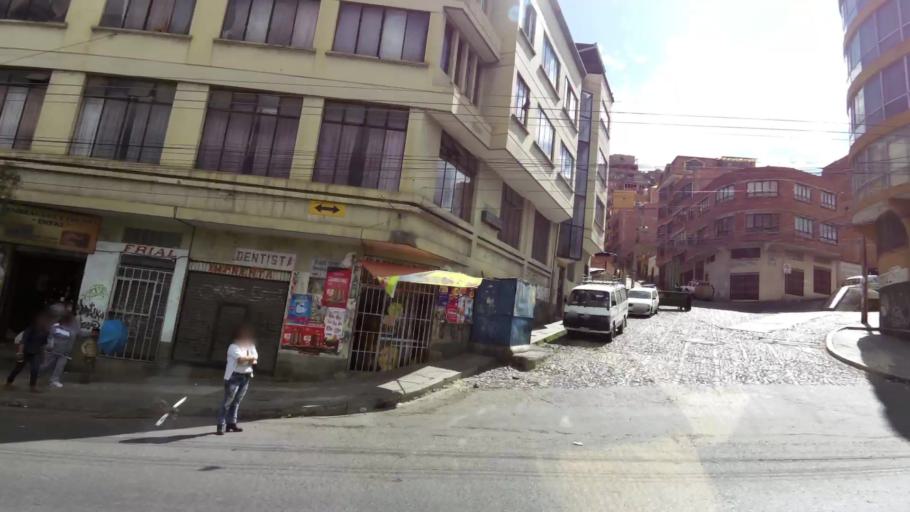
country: BO
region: La Paz
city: La Paz
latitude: -16.4861
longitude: -68.1243
